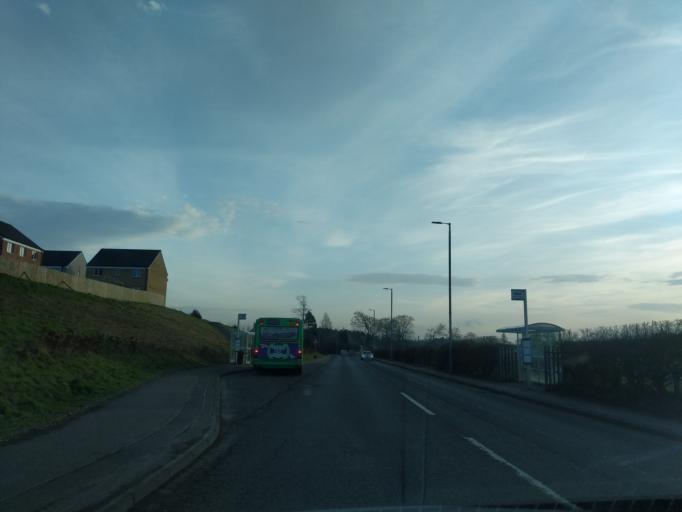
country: GB
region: Scotland
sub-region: South Lanarkshire
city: Carluke
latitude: 55.7256
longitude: -3.8324
